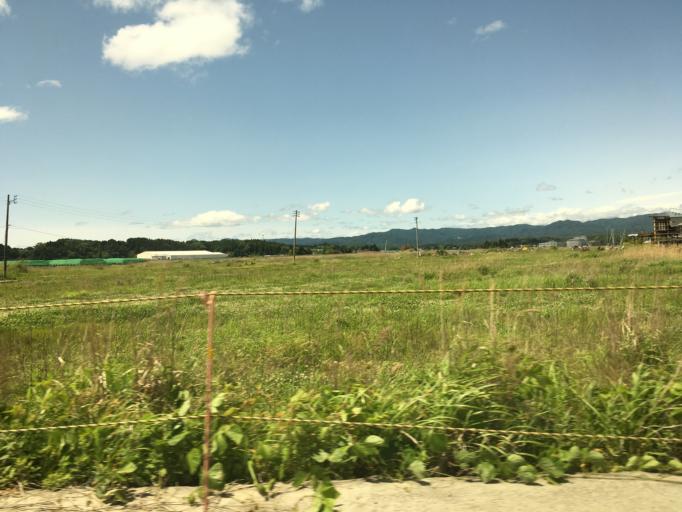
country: JP
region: Fukushima
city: Namie
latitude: 37.4598
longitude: 141.0311
